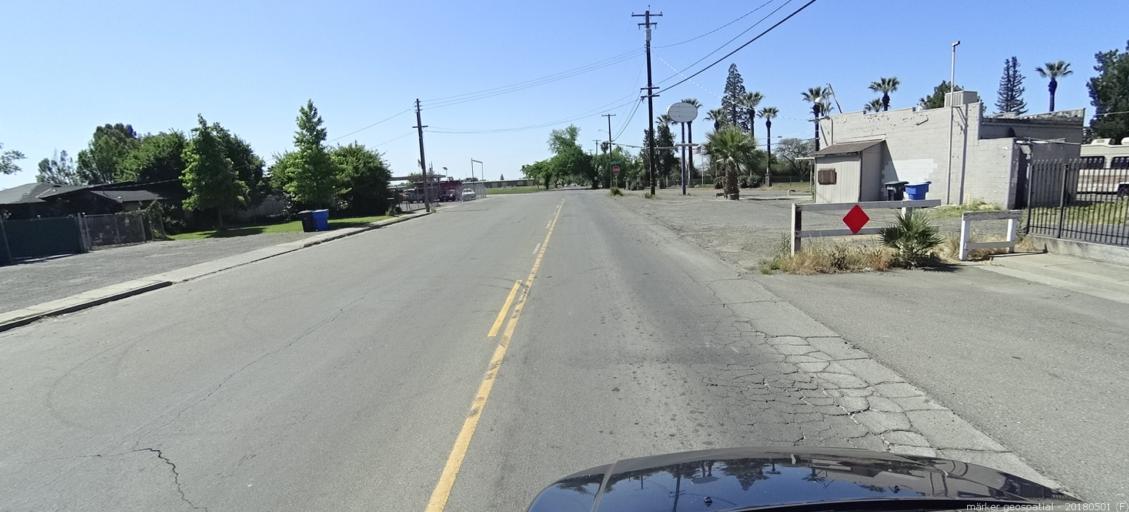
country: US
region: California
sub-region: Sacramento County
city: Rio Linda
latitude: 38.6526
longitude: -121.4385
